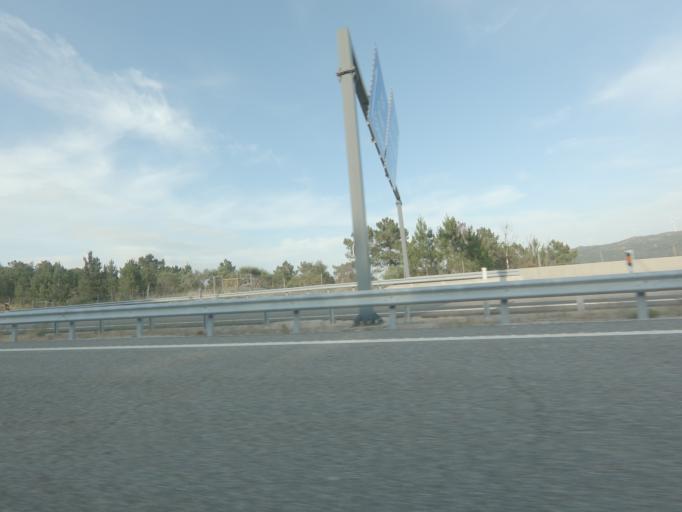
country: PT
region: Vila Real
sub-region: Vila Pouca de Aguiar
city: Vila Pouca de Aguiar
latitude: 41.5001
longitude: -7.6558
